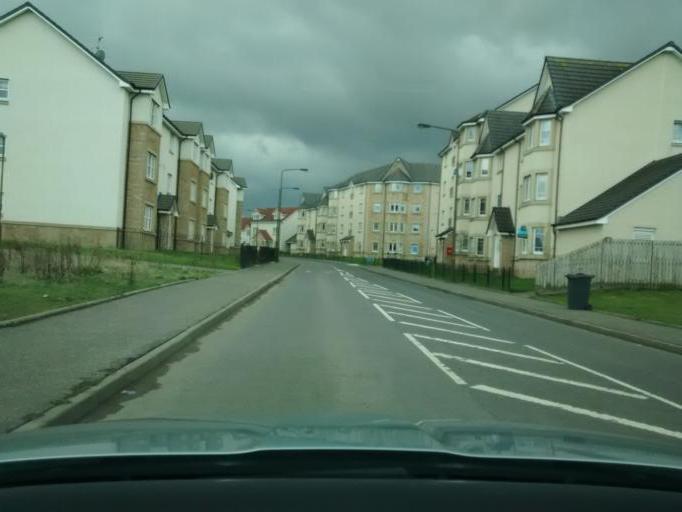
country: GB
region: Scotland
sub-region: West Lothian
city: Bathgate
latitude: 55.8878
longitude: -3.6414
